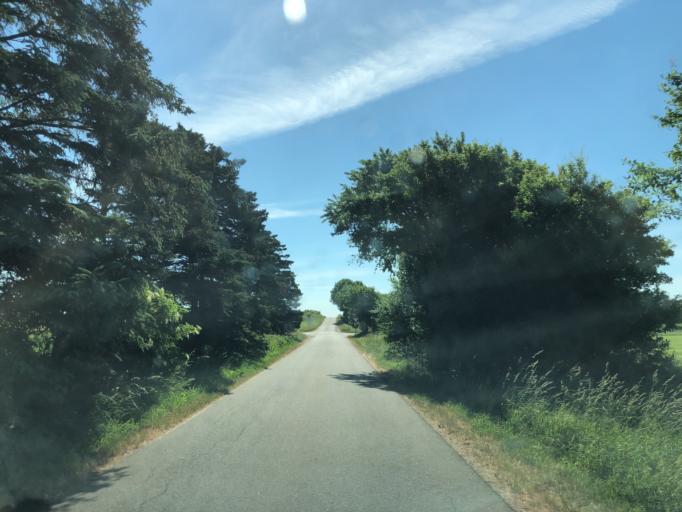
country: DK
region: Central Jutland
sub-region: Struer Kommune
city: Struer
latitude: 56.4294
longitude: 8.4614
